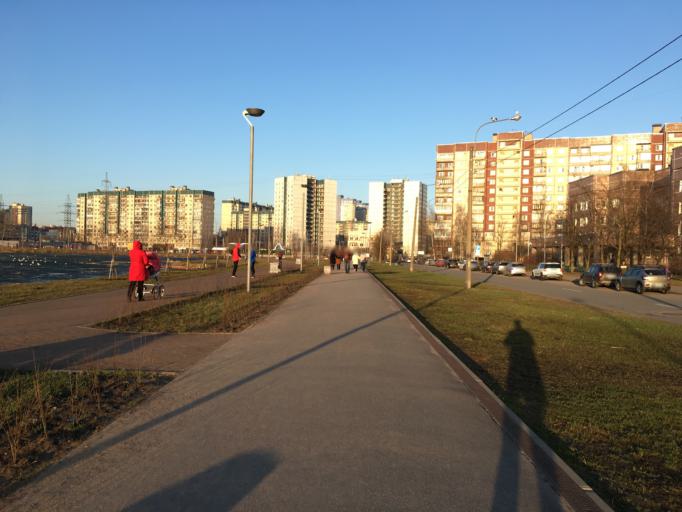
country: RU
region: St.-Petersburg
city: Komendantsky aerodrom
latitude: 60.0156
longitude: 30.2656
